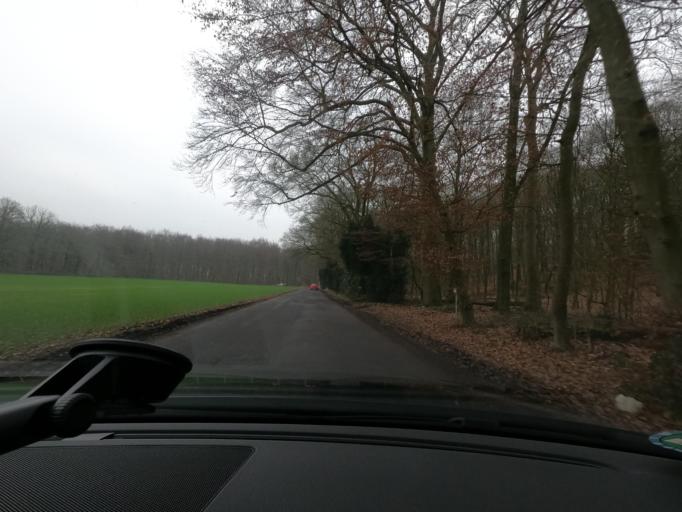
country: DE
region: North Rhine-Westphalia
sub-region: Regierungsbezirk Dusseldorf
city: Krefeld
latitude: 51.3900
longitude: 6.5426
